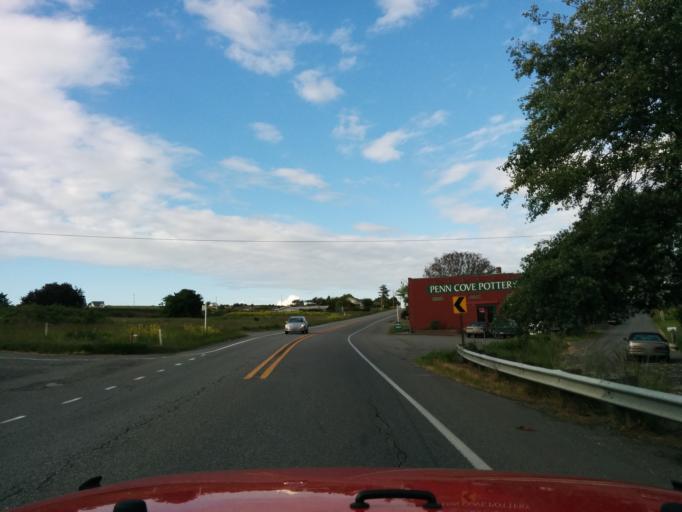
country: US
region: Washington
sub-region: Island County
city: Coupeville
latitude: 48.2347
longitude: -122.7238
